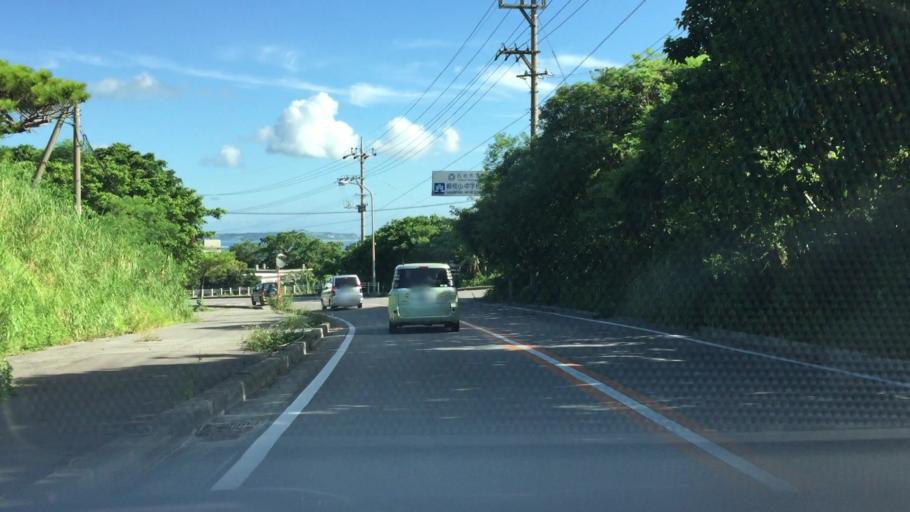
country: JP
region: Okinawa
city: Ishigaki
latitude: 24.4405
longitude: 124.1179
